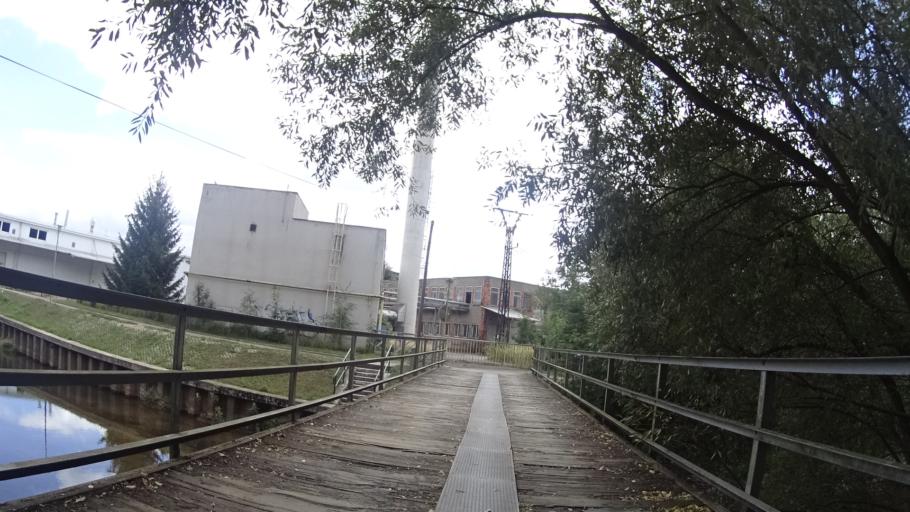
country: CZ
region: Pardubicky
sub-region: Okres Usti nad Orlici
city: Usti nad Orlici
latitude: 49.9751
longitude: 16.3863
